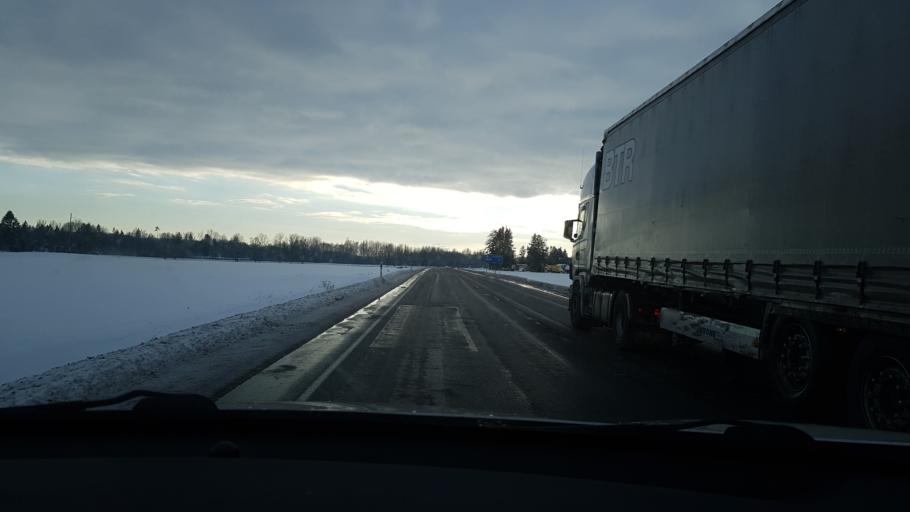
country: EE
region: Jaervamaa
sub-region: Paide linn
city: Paide
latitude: 58.9432
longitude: 25.6430
